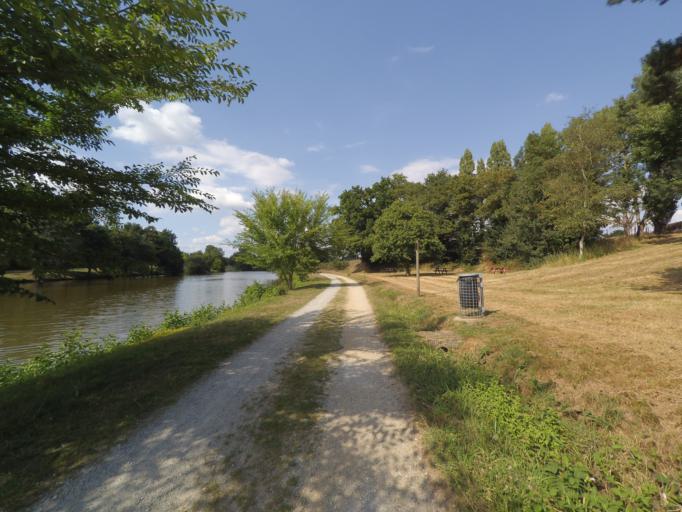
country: FR
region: Pays de la Loire
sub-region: Departement de la Loire-Atlantique
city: Vieillevigne
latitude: 46.9614
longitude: -1.4328
